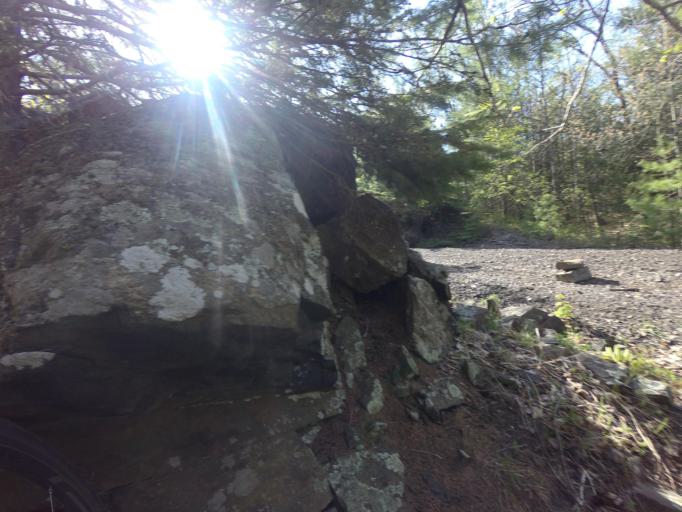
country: CA
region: Ontario
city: Arnprior
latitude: 45.4710
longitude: -76.3024
